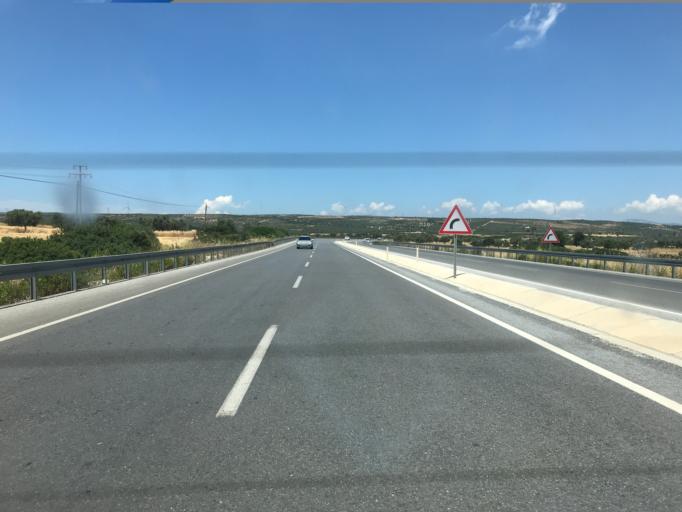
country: TR
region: Aydin
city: Akkoy
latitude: 37.4563
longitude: 27.3420
